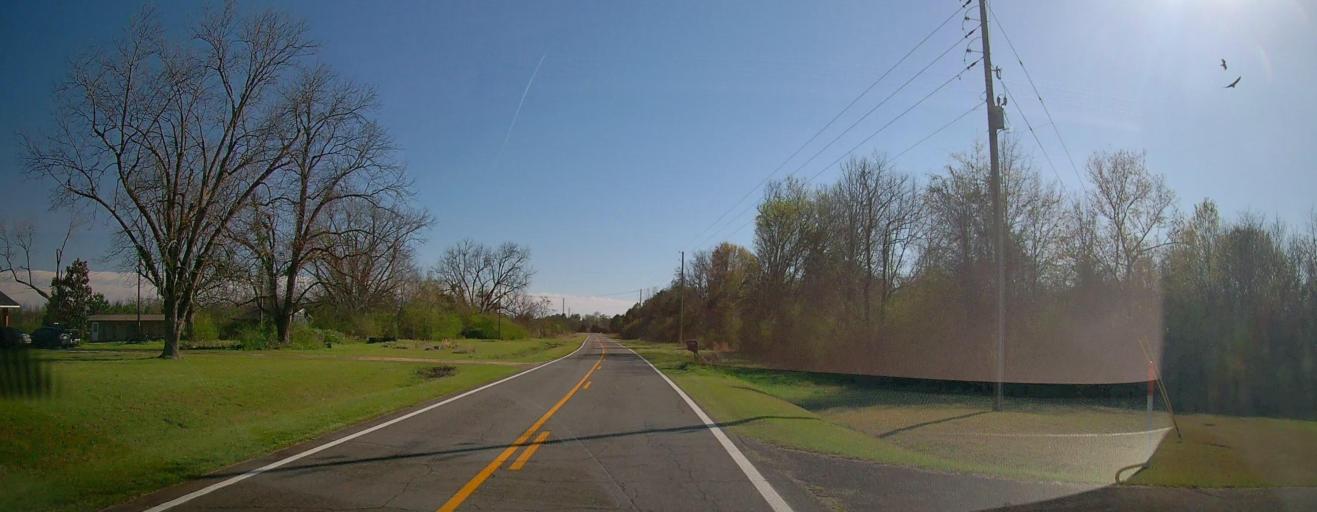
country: US
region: Georgia
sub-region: Peach County
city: Fort Valley
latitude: 32.5952
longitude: -83.9889
